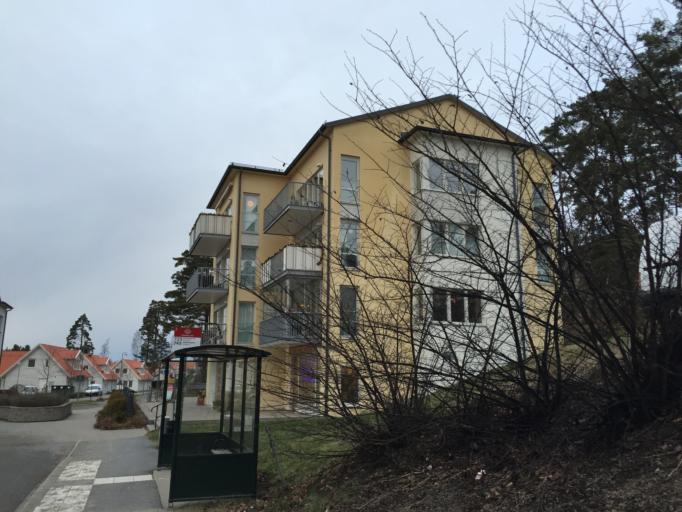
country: SE
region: Stockholm
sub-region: Botkyrka Kommun
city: Varsta
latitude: 59.2028
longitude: 17.7876
